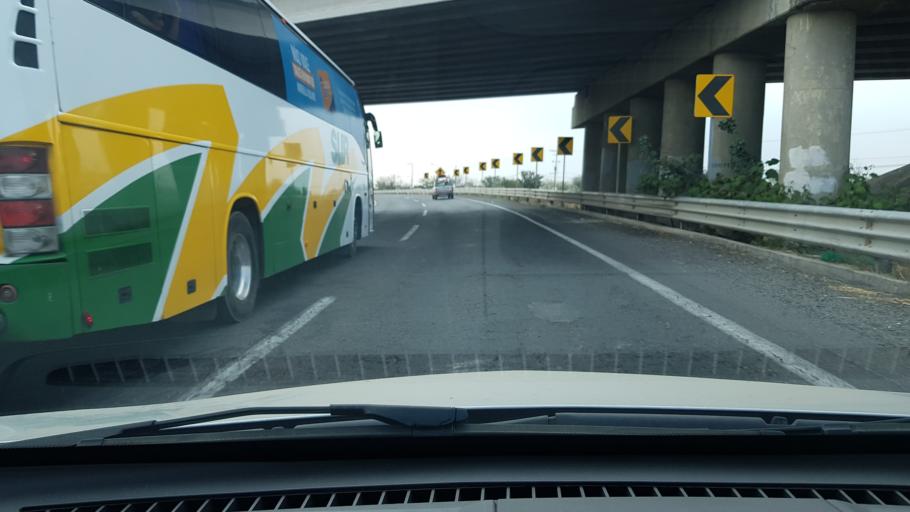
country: MX
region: Morelos
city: Amayuca
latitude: 18.7305
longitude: -98.8114
